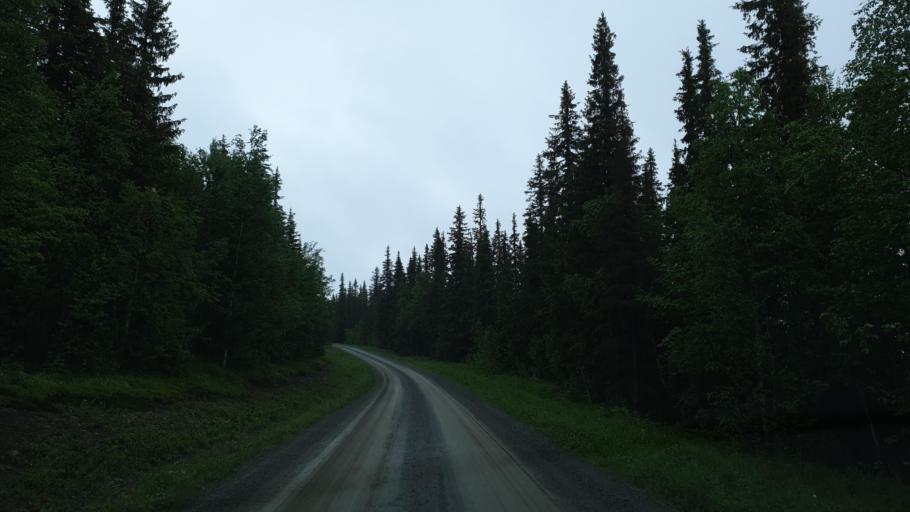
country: SE
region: Vaesterbotten
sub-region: Vilhelmina Kommun
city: Sjoberg
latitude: 65.3311
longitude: 15.9082
